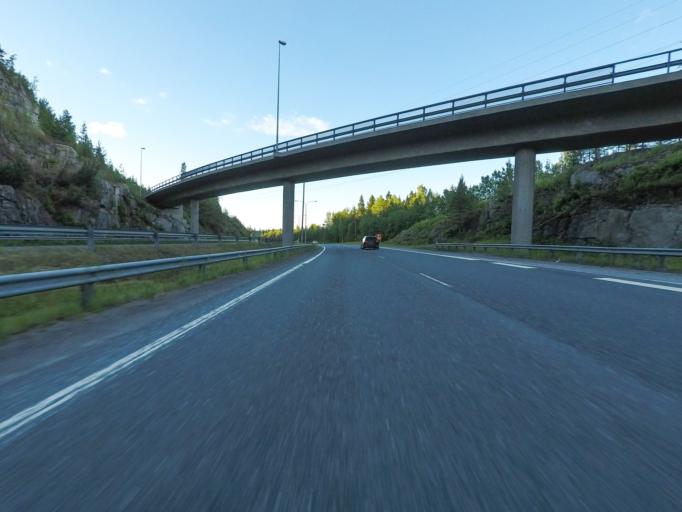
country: FI
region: Northern Savo
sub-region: Kuopio
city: Kuopio
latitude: 62.8456
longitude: 27.6159
